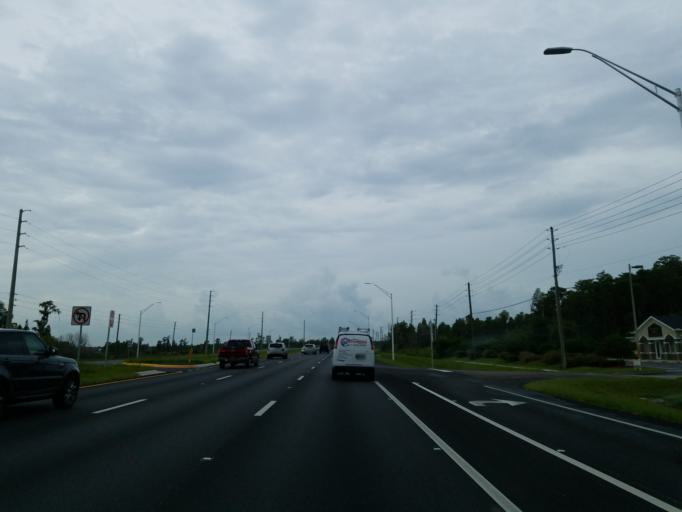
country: US
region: Florida
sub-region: Pasco County
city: Land O' Lakes
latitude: 28.1963
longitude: -82.4949
